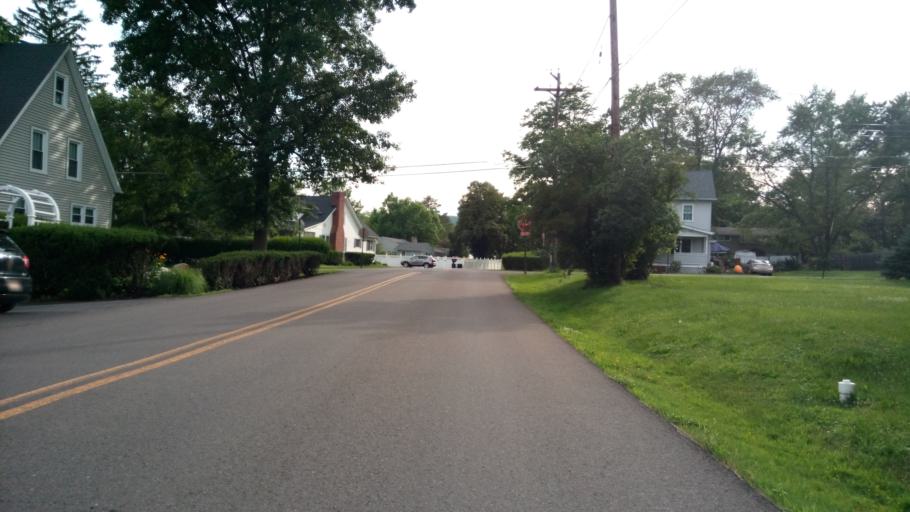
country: US
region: New York
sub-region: Chemung County
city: West Elmira
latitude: 42.0846
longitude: -76.8398
